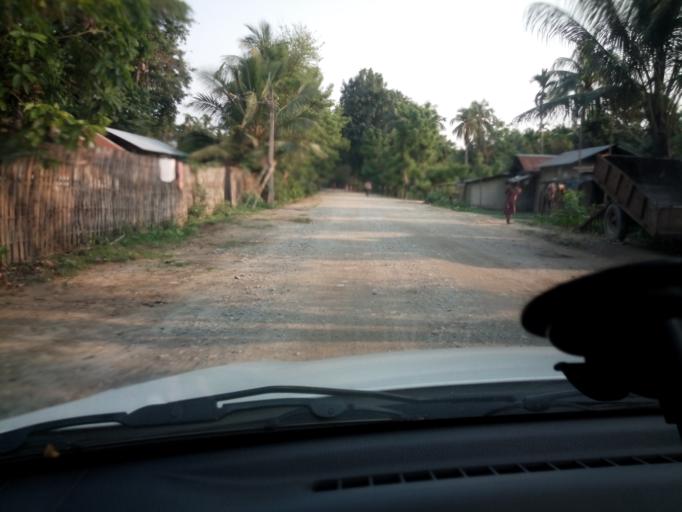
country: IN
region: Assam
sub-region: Udalguri
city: Udalguri
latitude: 26.7281
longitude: 92.0853
